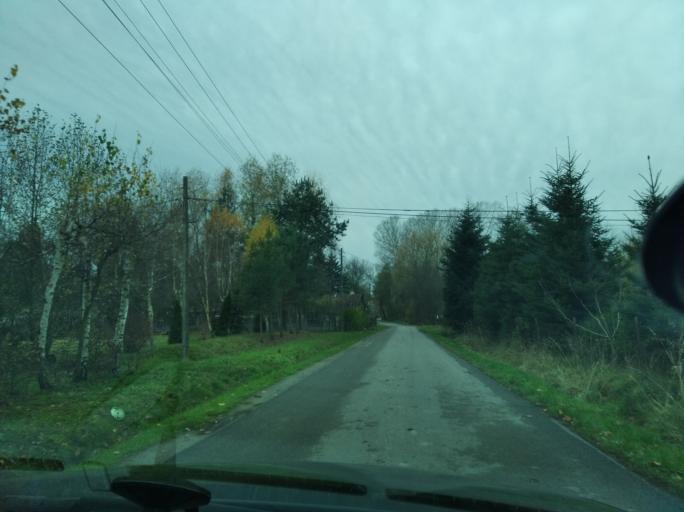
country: PL
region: Subcarpathian Voivodeship
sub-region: Powiat lancucki
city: Markowa
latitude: 50.0232
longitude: 22.3279
